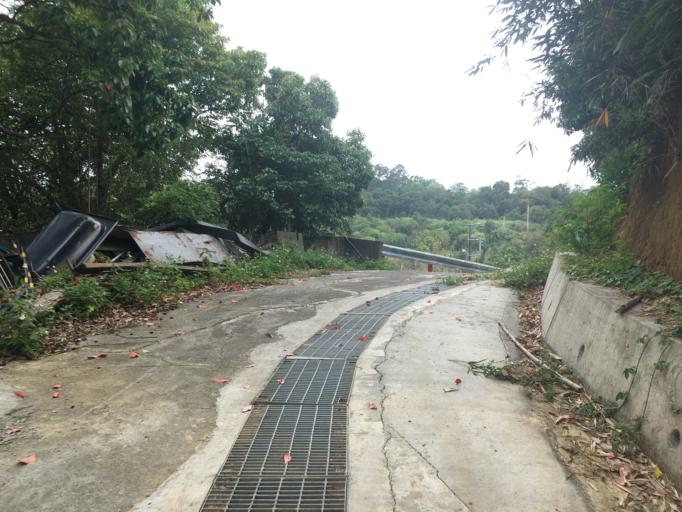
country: TW
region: Taiwan
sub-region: Hsinchu
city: Hsinchu
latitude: 24.7428
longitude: 120.9780
